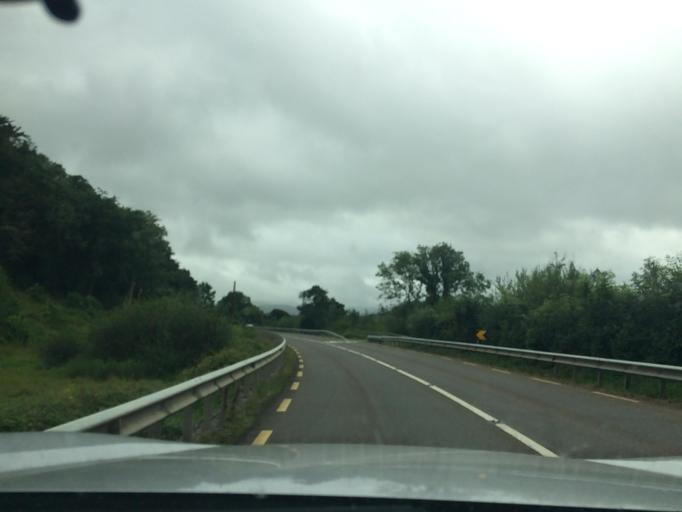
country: IE
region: Munster
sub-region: South Tipperary
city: Cluain Meala
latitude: 52.3115
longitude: -7.7894
